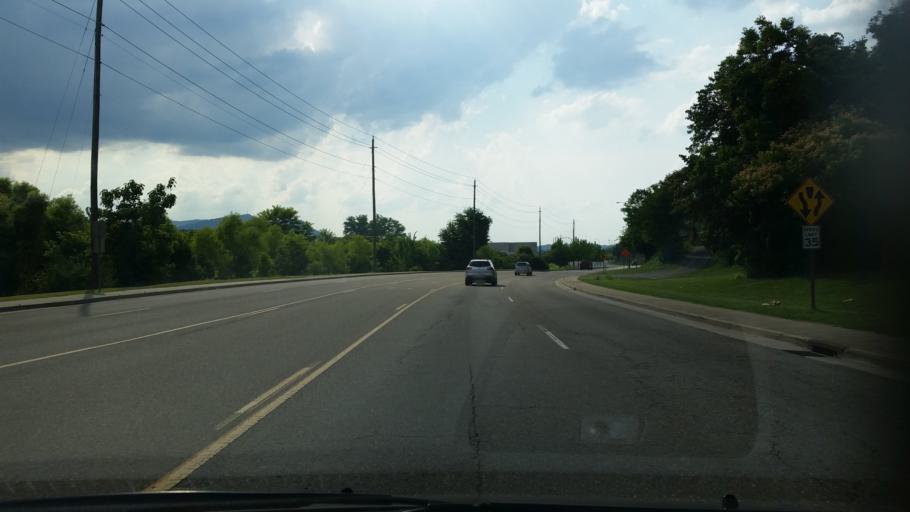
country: US
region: Tennessee
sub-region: Sevier County
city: Pigeon Forge
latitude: 35.7950
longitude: -83.5559
